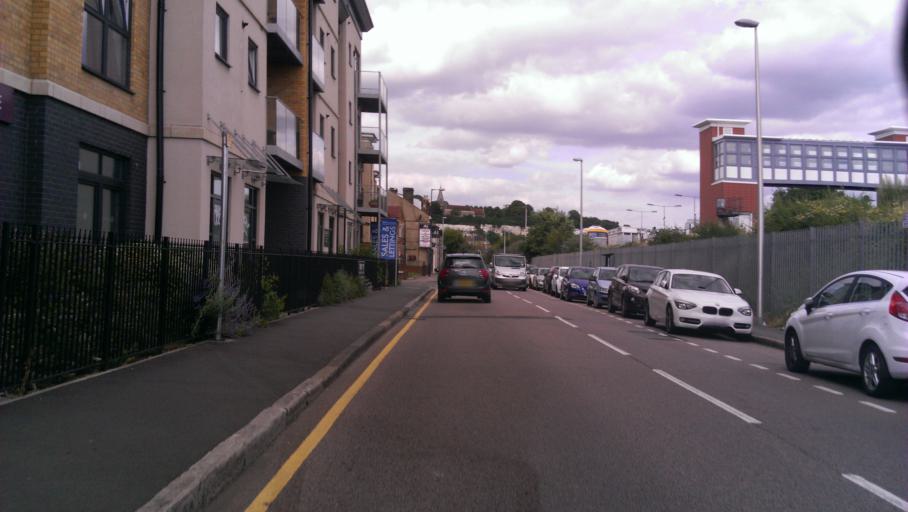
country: GB
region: England
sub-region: Kent
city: Strood
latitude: 51.3959
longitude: 0.4987
